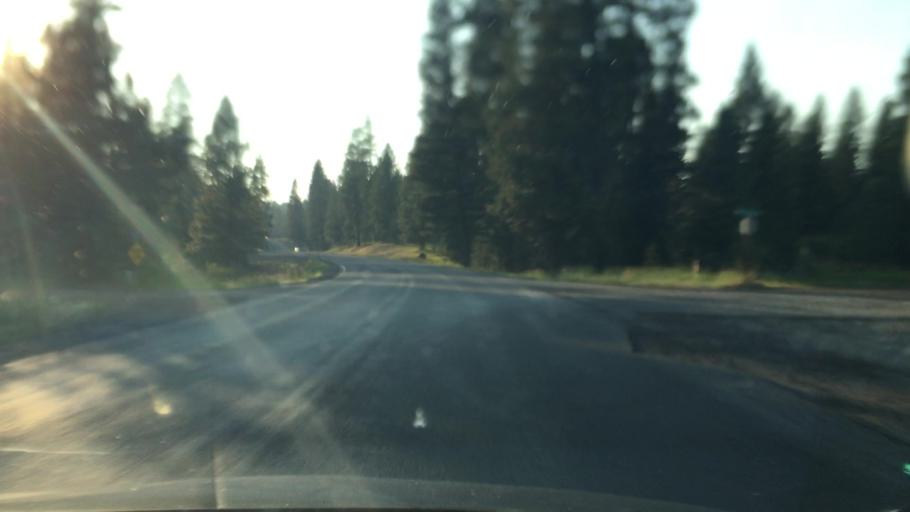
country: US
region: Idaho
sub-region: Valley County
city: McCall
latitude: 44.9252
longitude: -116.1427
